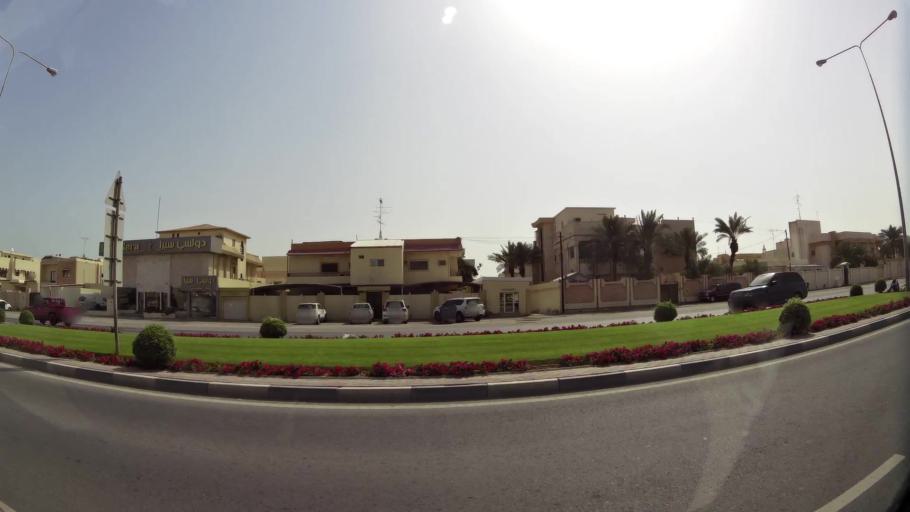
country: QA
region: Baladiyat ad Dawhah
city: Doha
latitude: 25.2490
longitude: 51.5242
